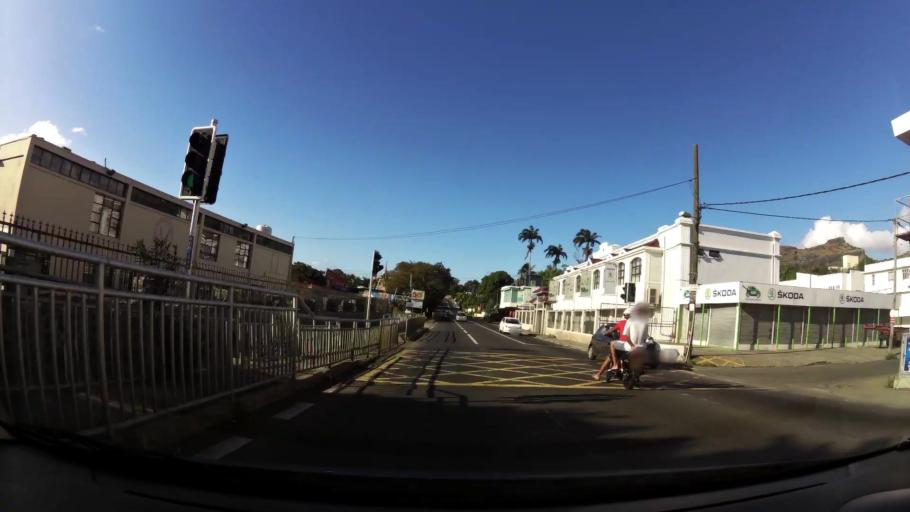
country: MU
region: Moka
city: Pailles
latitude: -20.1733
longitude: 57.4752
